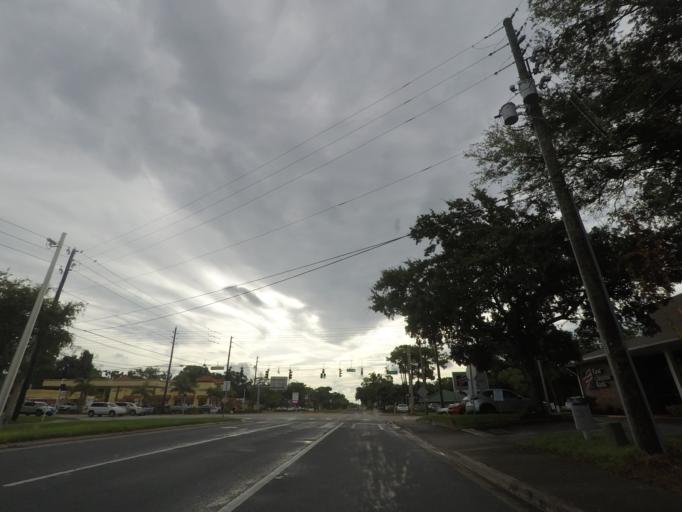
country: US
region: Florida
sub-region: Pinellas County
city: Redington Shores
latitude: 27.8437
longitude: -82.8287
